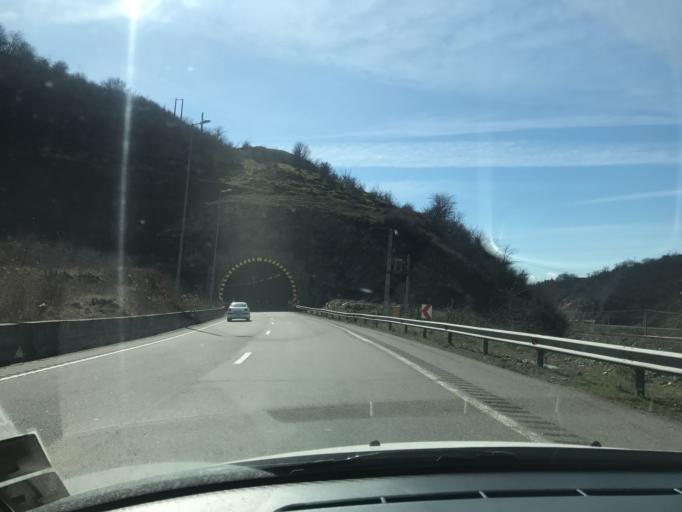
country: IR
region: Gilan
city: Pa'in-e Bazar-e Rudbar
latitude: 36.9526
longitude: 49.5496
